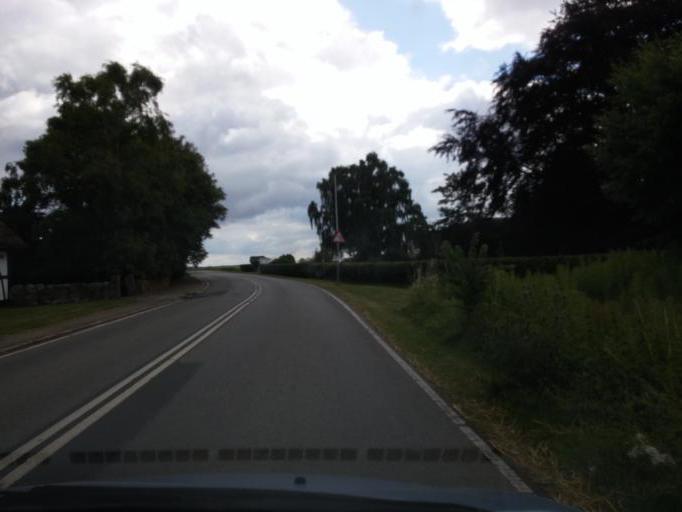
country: DK
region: South Denmark
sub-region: Kerteminde Kommune
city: Kerteminde
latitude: 55.4302
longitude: 10.6246
